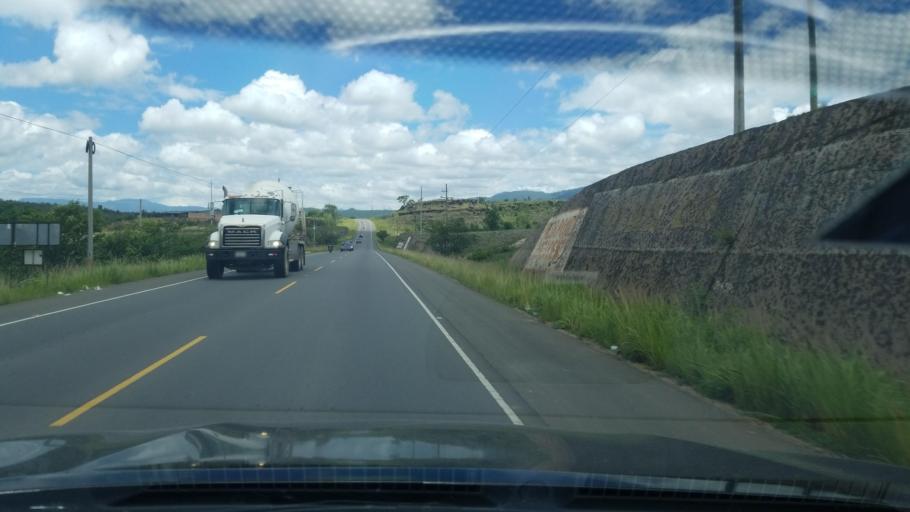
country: HN
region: Francisco Morazan
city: Cofradia
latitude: 14.3061
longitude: -87.2234
